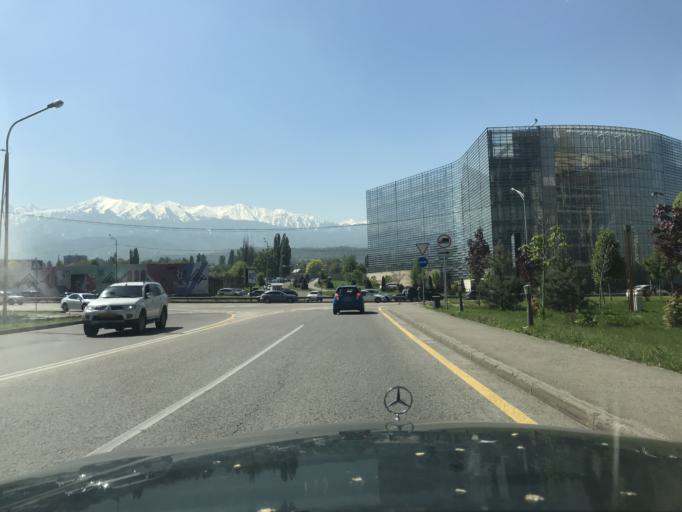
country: KZ
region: Almaty Qalasy
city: Almaty
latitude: 43.2286
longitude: 76.9443
